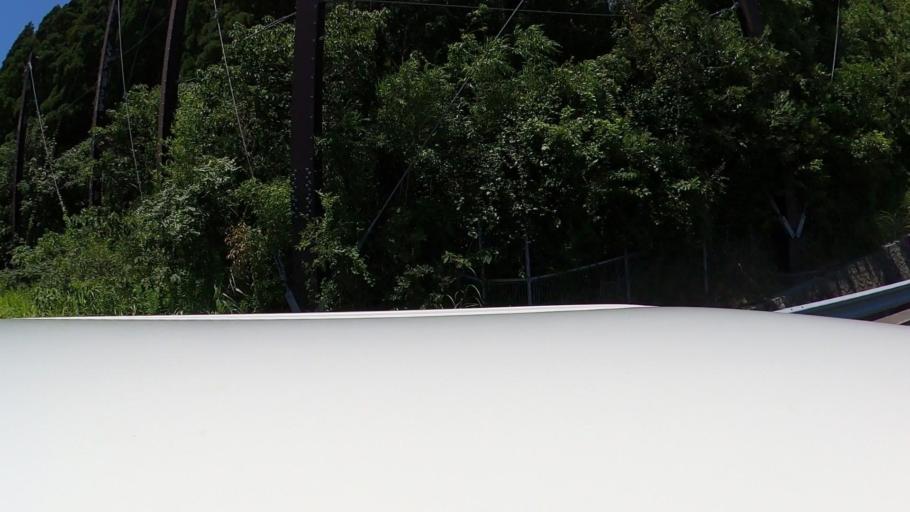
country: JP
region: Miyazaki
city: Nobeoka
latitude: 32.3879
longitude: 131.6218
